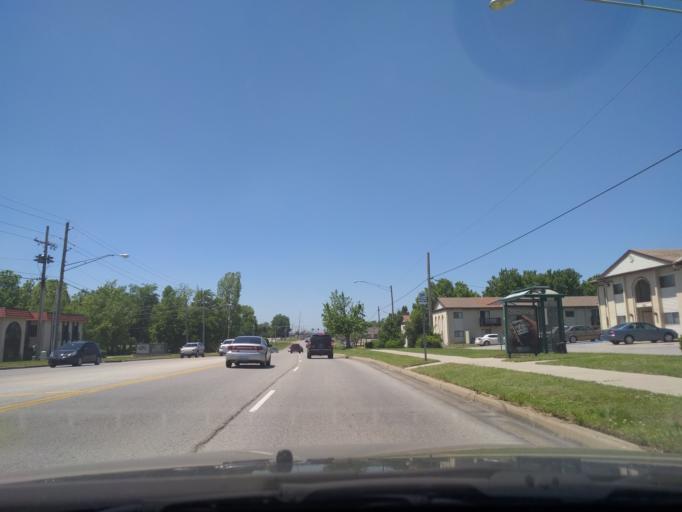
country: US
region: Oklahoma
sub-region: Tulsa County
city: Broken Arrow
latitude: 36.0610
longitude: -95.8058
